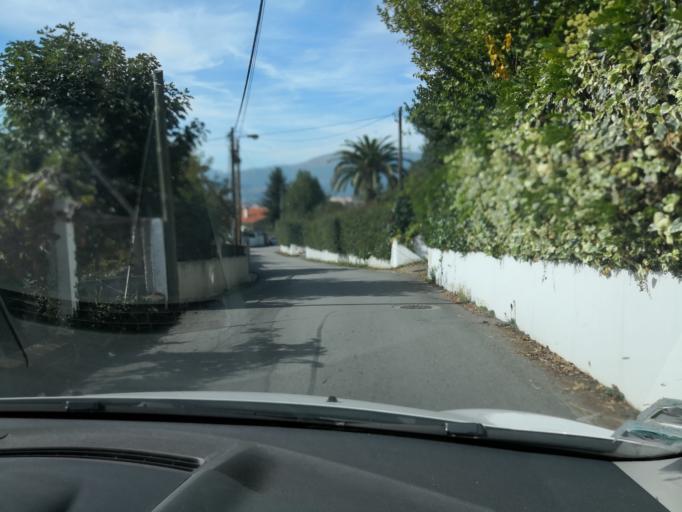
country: PT
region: Vila Real
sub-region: Vila Real
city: Vila Real
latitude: 41.2980
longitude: -7.7268
